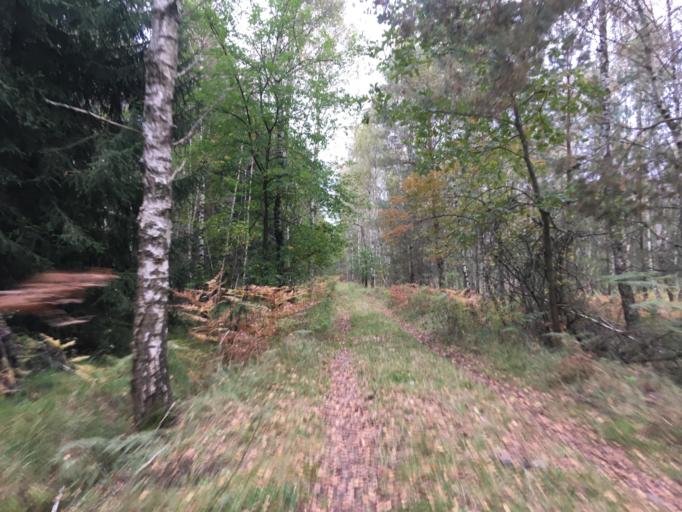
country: DE
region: Brandenburg
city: Birkenwerder
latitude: 52.6960
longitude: 13.3483
